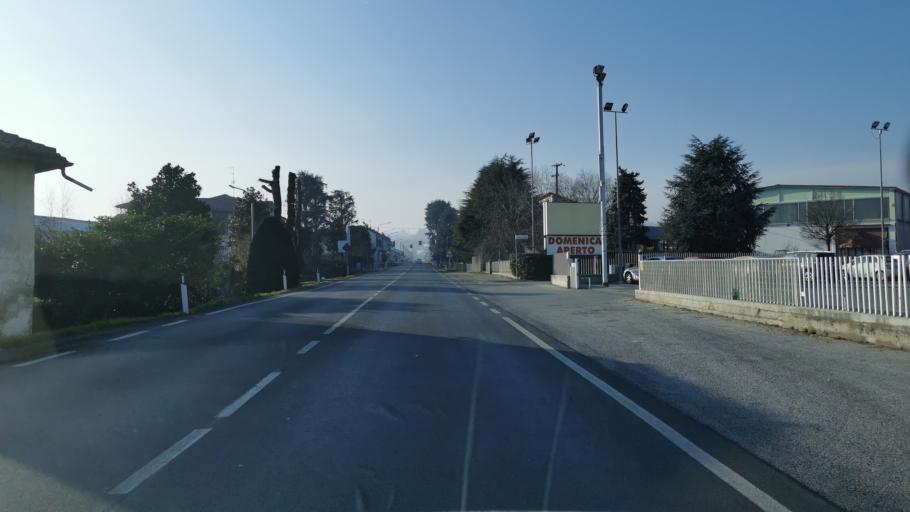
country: IT
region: Piedmont
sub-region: Provincia di Cuneo
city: Pocapaglia
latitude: 44.6969
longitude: 7.8905
